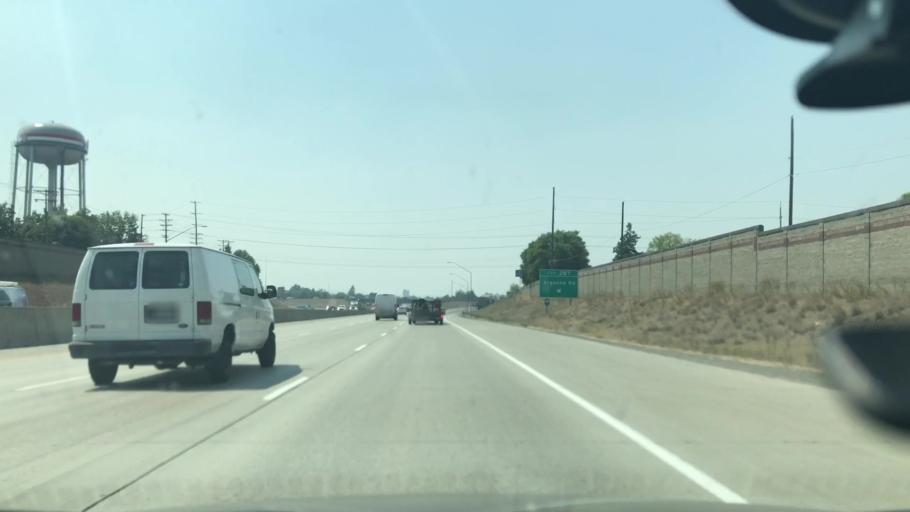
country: US
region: Washington
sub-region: Spokane County
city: Millwood
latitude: 47.6748
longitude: -117.2752
